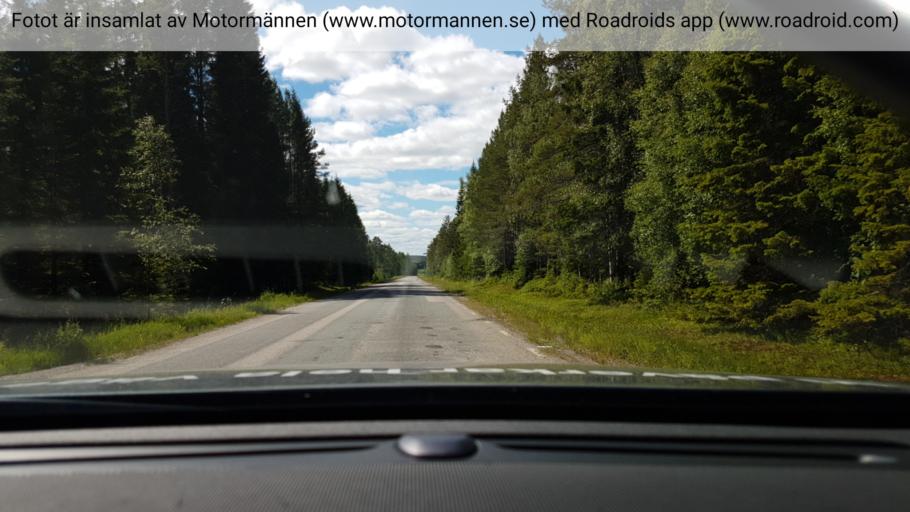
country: SE
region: Vaesterbotten
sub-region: Skelleftea Kommun
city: Burea
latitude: 64.3978
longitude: 21.3361
